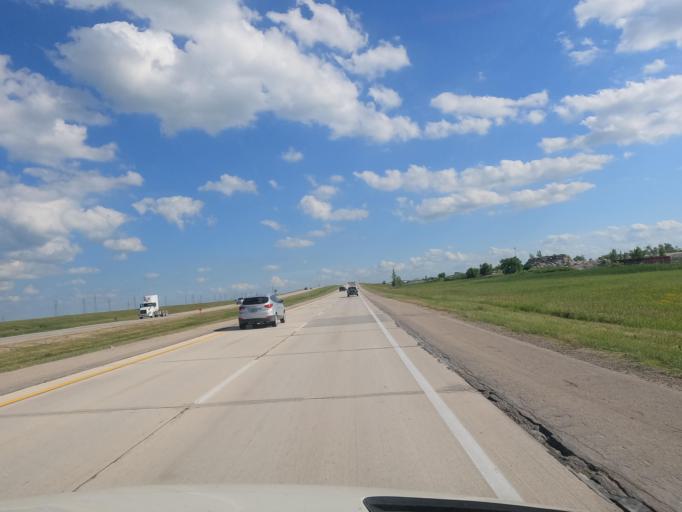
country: CA
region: Manitoba
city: Winnipeg
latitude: 49.9302
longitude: -96.9752
